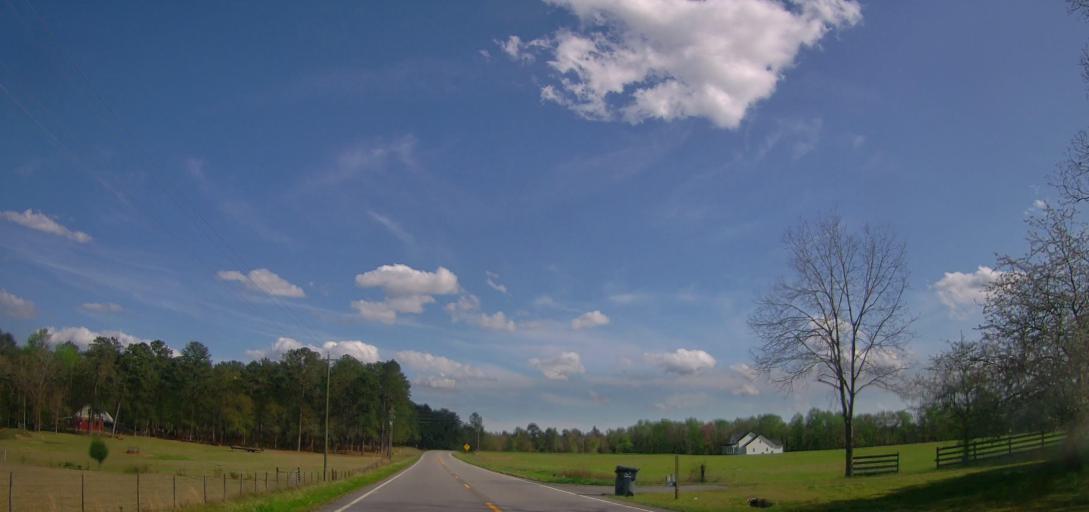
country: US
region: Georgia
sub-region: Baldwin County
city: Hardwick
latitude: 33.0577
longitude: -83.1272
